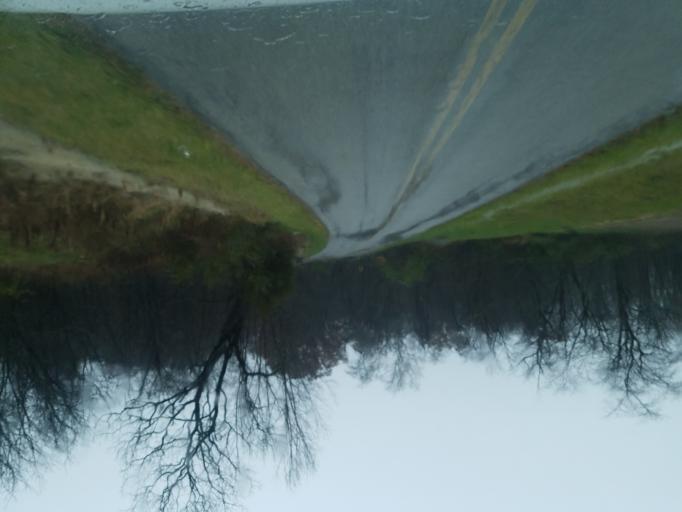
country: US
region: Ohio
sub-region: Delaware County
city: Ashley
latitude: 40.3548
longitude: -82.8825
